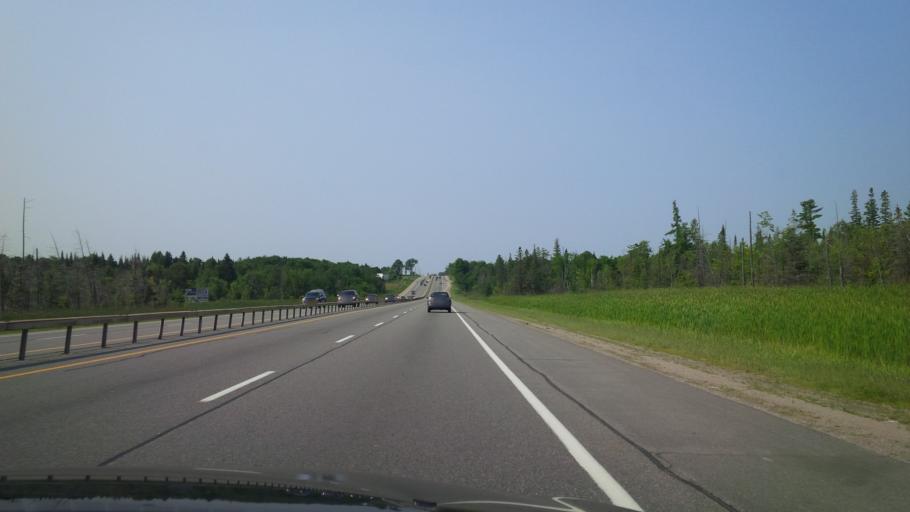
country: CA
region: Ontario
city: Orillia
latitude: 44.5407
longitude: -79.4556
